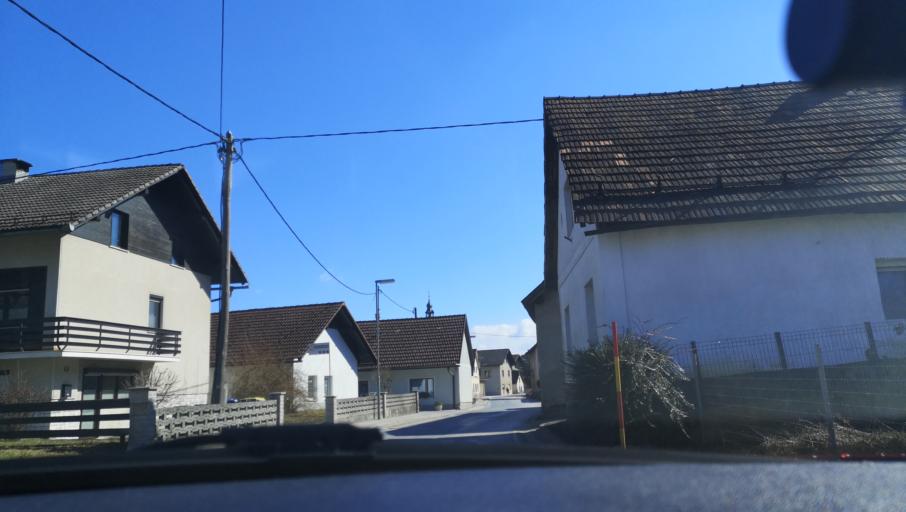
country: SI
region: Ig
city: Ig
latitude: 45.9608
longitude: 14.5232
